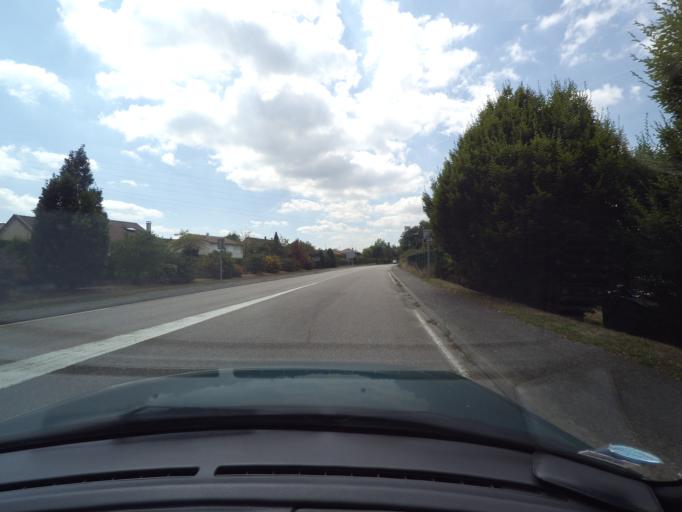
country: FR
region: Limousin
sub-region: Departement de la Haute-Vienne
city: Isle
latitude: 45.7893
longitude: 1.2400
